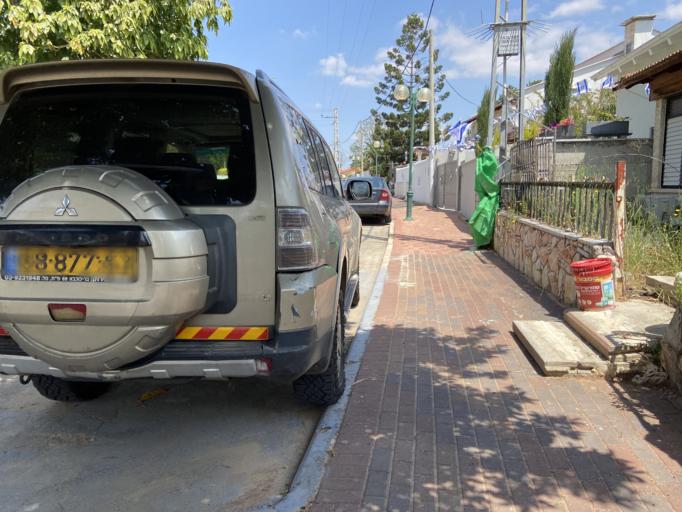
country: IL
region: Central District
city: Kfar Saba
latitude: 32.1577
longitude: 34.9251
